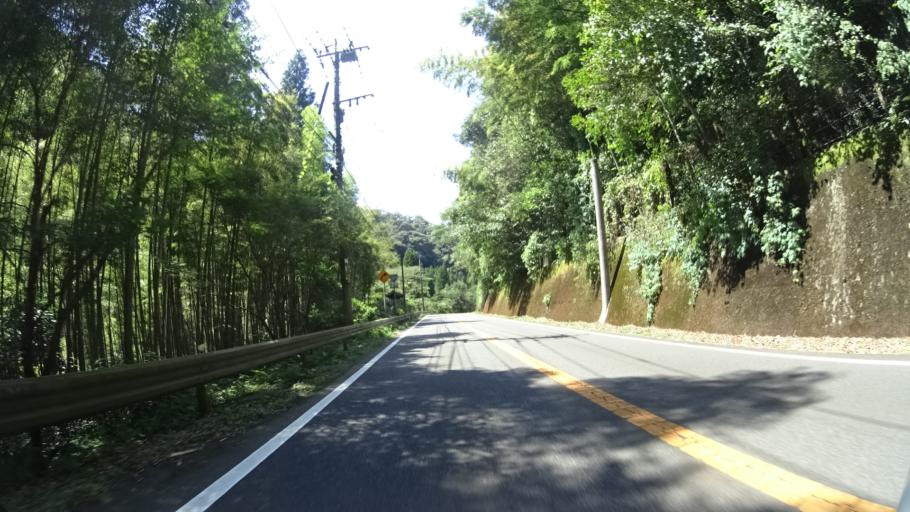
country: JP
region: Kagoshima
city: Kokubu-matsuki
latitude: 31.8327
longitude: 130.7424
